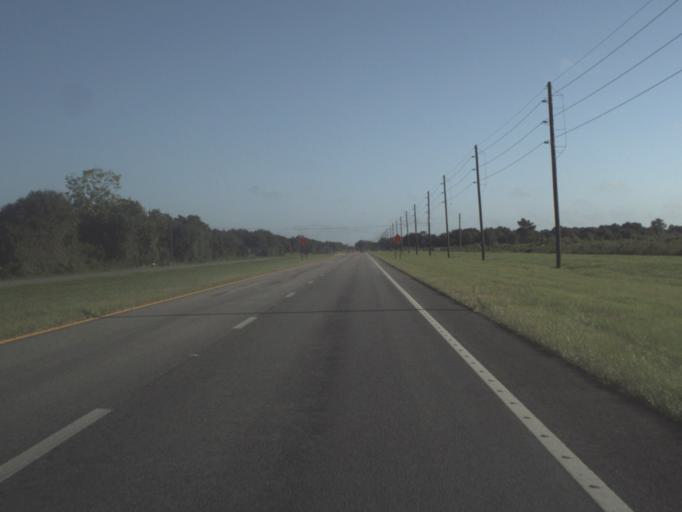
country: US
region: Florida
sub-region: DeSoto County
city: Nocatee
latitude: 27.1411
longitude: -81.8963
